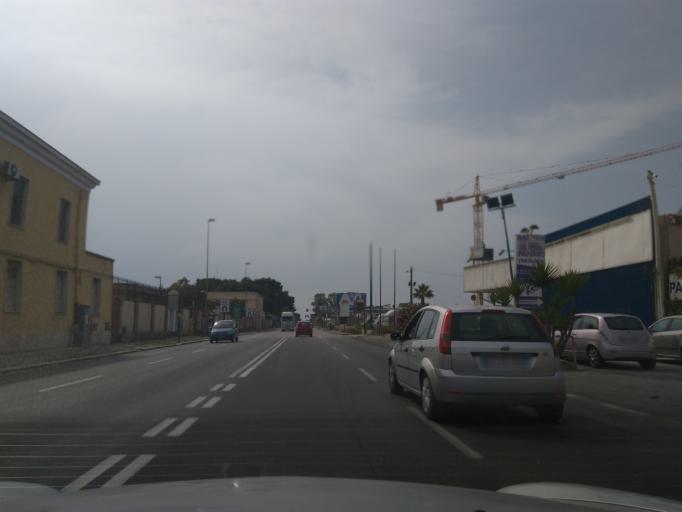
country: IT
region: Apulia
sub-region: Provincia di Bari
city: Bari
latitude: 41.1287
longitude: 16.8362
